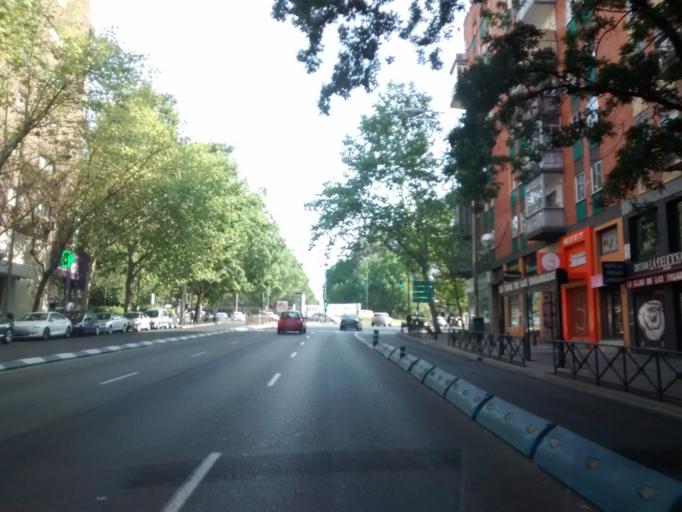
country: ES
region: Madrid
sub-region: Provincia de Madrid
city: Arganzuela
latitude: 40.4001
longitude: -3.7001
